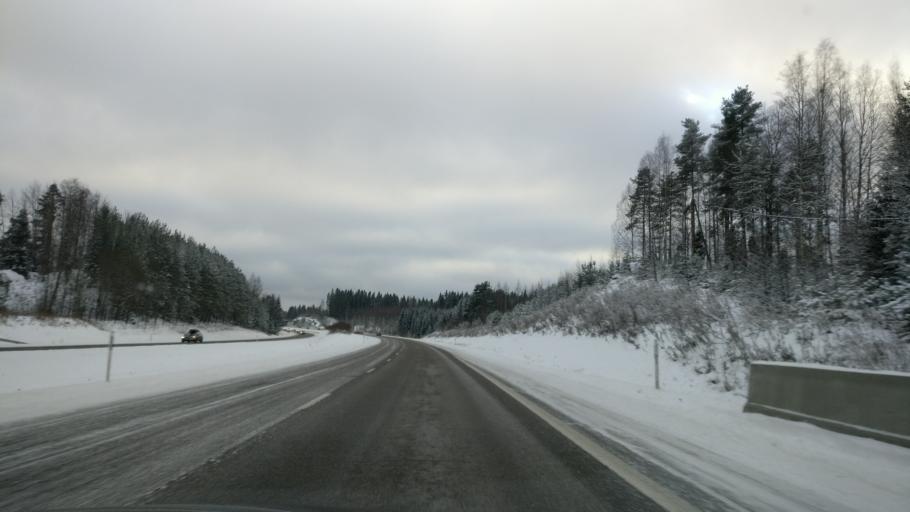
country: FI
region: Paijanne Tavastia
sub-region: Lahti
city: Nastola
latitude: 61.0942
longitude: 25.8985
